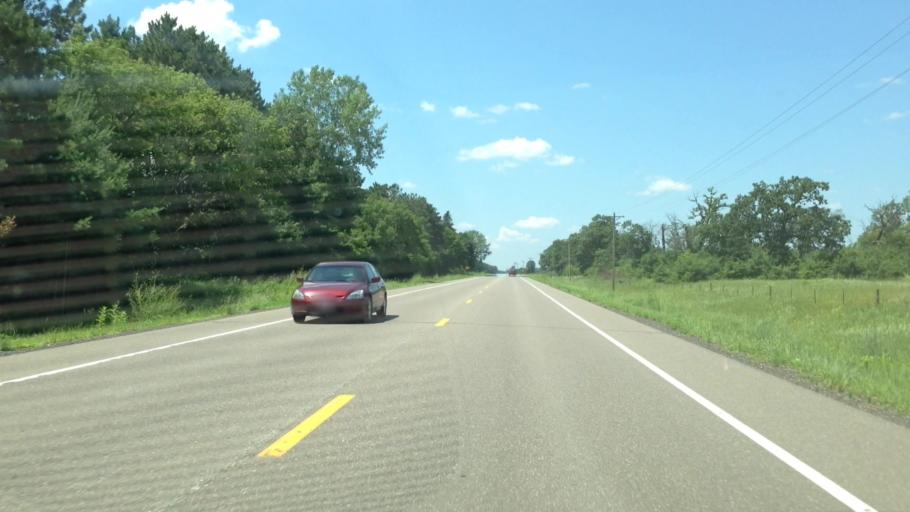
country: US
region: Minnesota
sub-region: Sherburne County
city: Zimmerman
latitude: 45.4439
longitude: -93.6688
